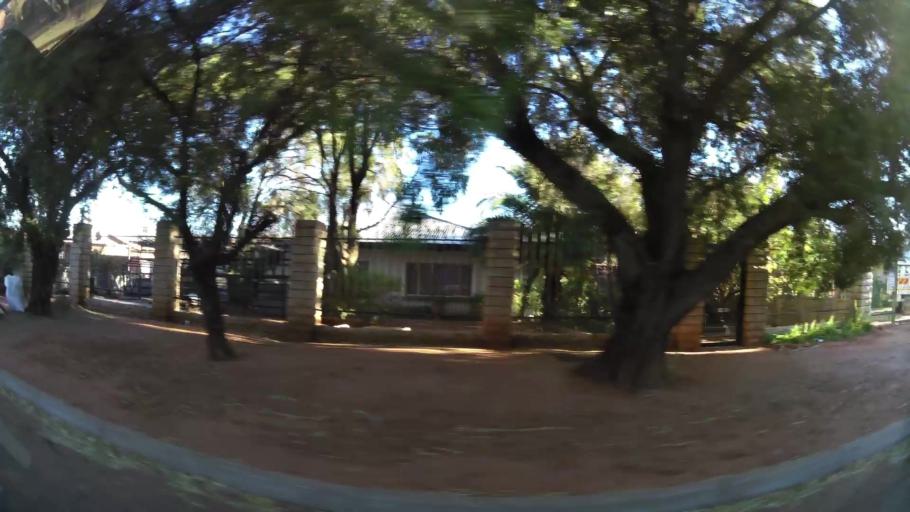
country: ZA
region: Northern Cape
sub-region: Frances Baard District Municipality
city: Kimberley
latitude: -28.7479
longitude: 24.7462
